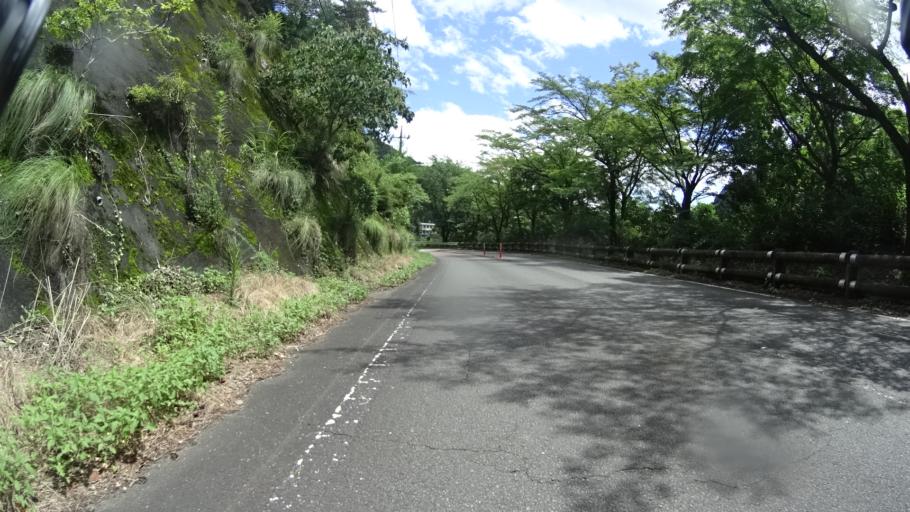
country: JP
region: Tokyo
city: Ome
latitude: 35.8748
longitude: 139.1718
